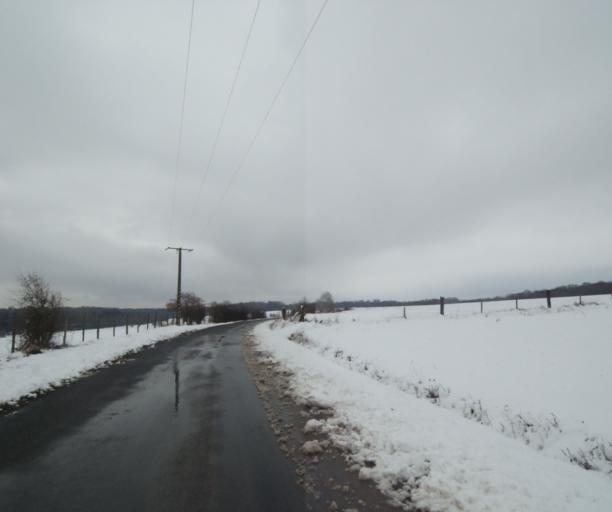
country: FR
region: Champagne-Ardenne
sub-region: Departement de la Haute-Marne
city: Laneuville-a-Remy
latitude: 48.4769
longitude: 4.8819
